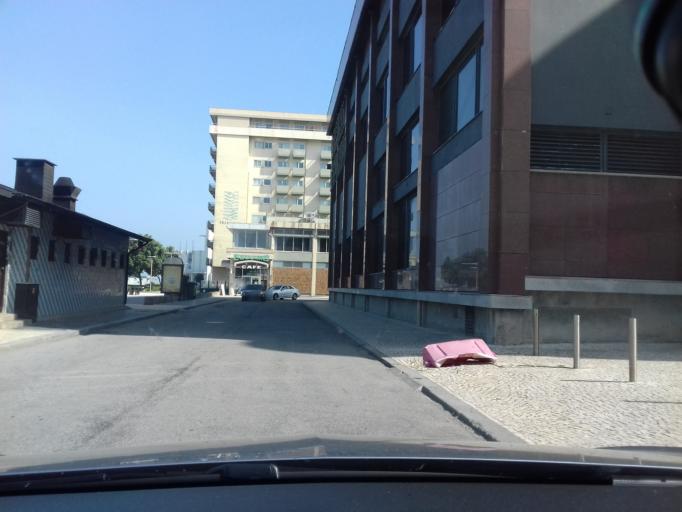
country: PT
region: Aveiro
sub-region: Espinho
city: Espinho
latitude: 41.0085
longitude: -8.6453
